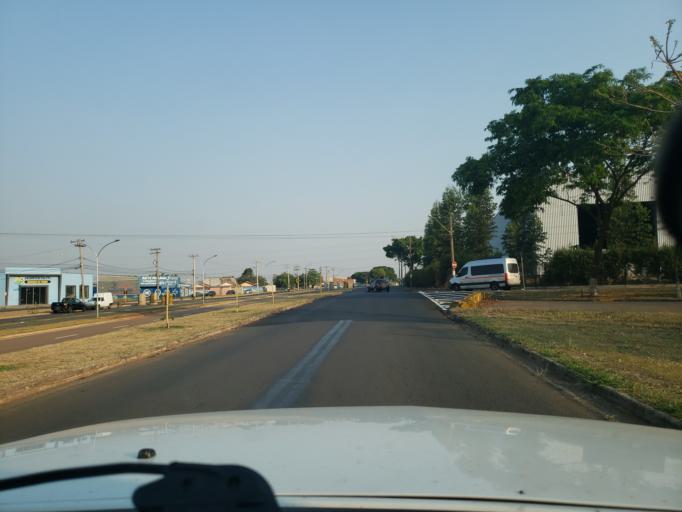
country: BR
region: Sao Paulo
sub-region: Moji-Guacu
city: Mogi-Gaucu
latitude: -22.3376
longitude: -46.9441
